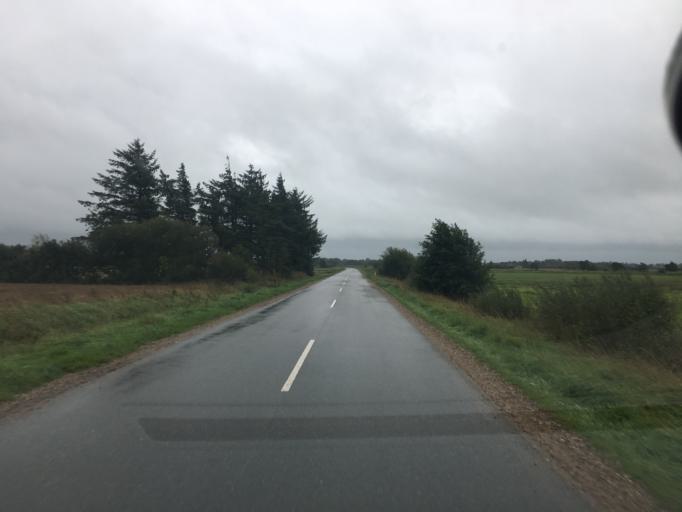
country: DE
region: Schleswig-Holstein
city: Bramstedtlund
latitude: 54.9720
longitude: 9.0439
